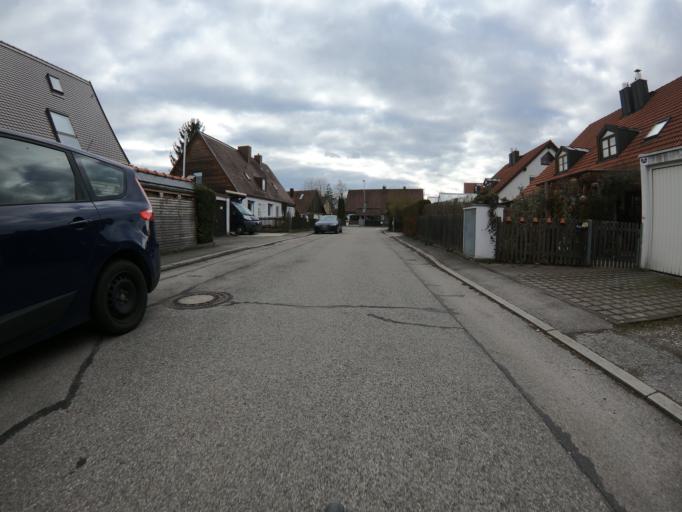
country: DE
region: Bavaria
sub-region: Upper Bavaria
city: Fuerstenfeldbruck
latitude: 48.1869
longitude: 11.2593
